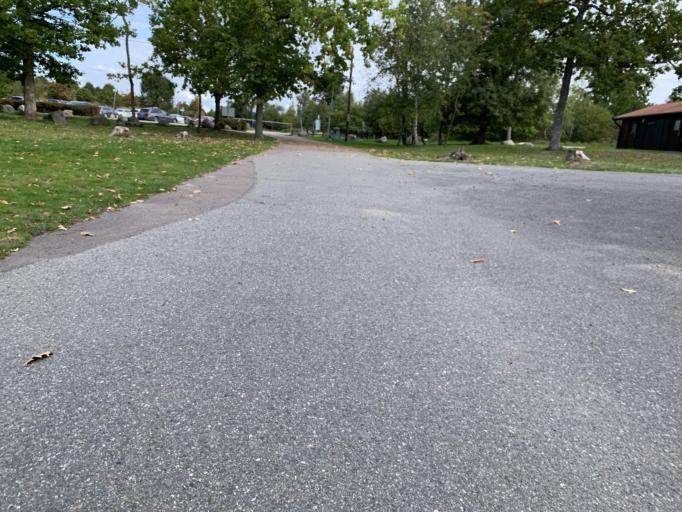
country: SE
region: Vaestmanland
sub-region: Vasteras
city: Vasteras
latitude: 59.5674
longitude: 16.6213
